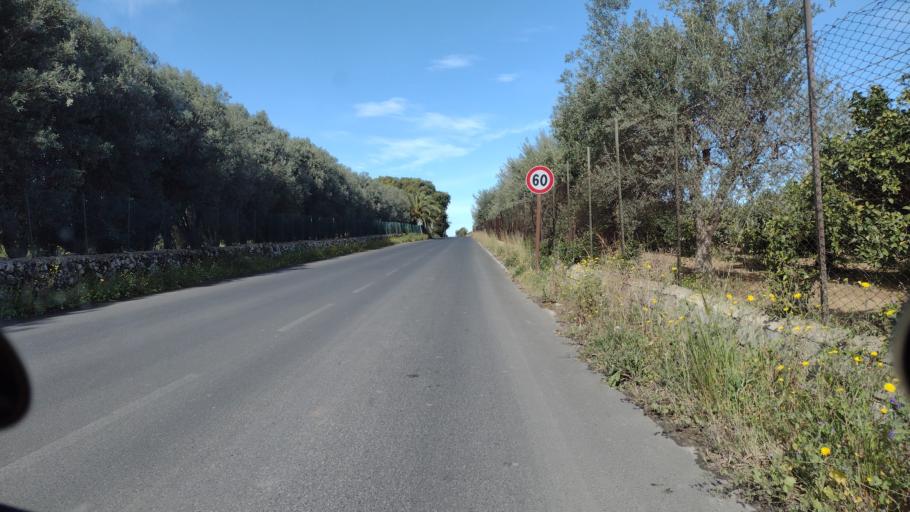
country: IT
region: Sicily
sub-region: Provincia di Siracusa
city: Noto
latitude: 36.8761
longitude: 15.1033
